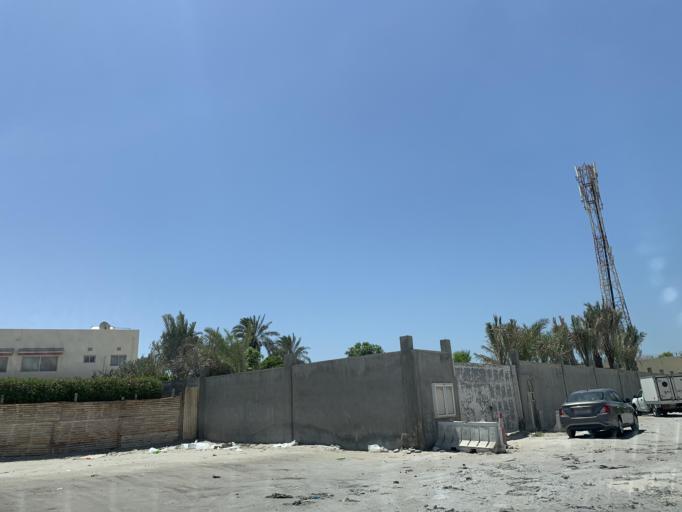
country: BH
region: Manama
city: Jidd Hafs
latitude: 26.2206
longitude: 50.4888
